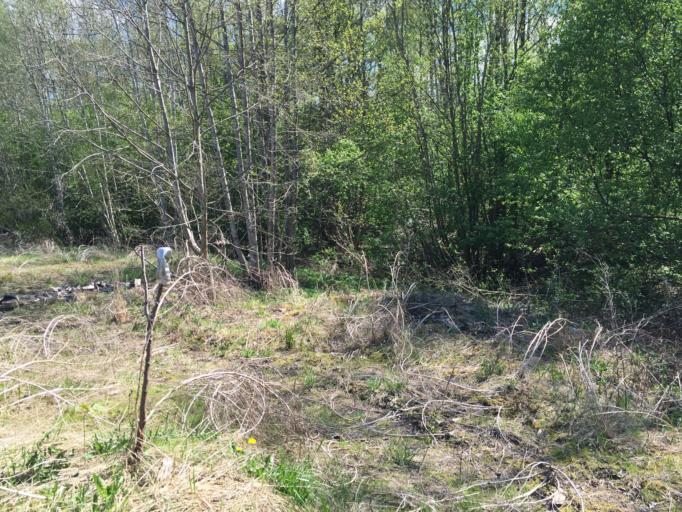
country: LV
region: Saulkrastu
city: Saulkrasti
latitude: 57.3235
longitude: 24.4880
